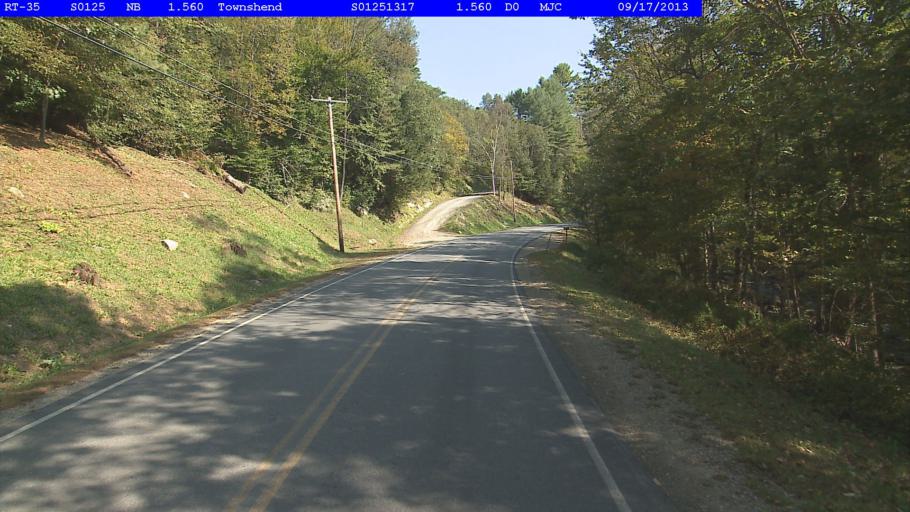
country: US
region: Vermont
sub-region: Windham County
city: Newfane
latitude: 43.0679
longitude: -72.6606
